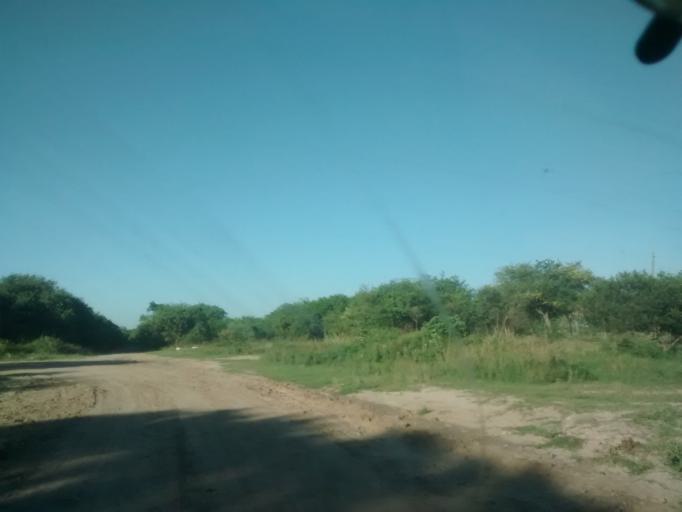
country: AR
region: Chaco
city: Resistencia
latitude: -27.4718
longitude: -59.0382
